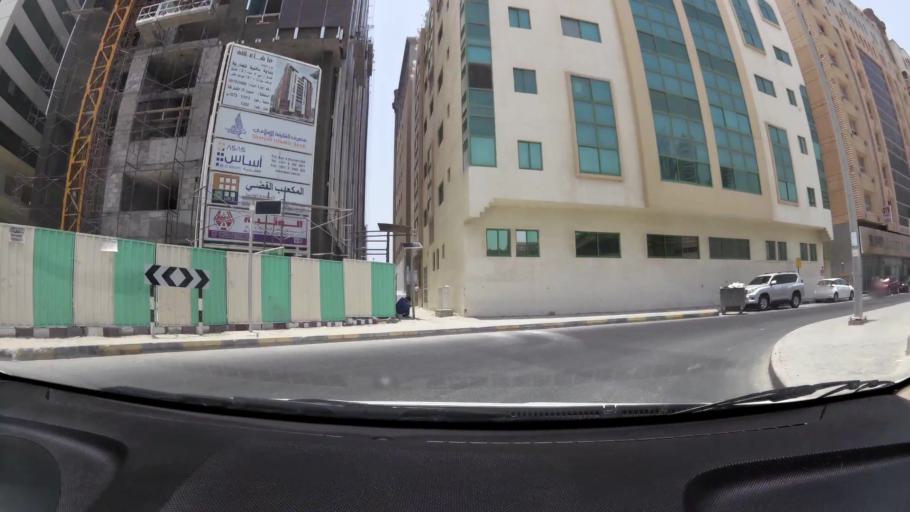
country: AE
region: Ash Shariqah
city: Sharjah
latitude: 25.3314
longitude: 55.3711
